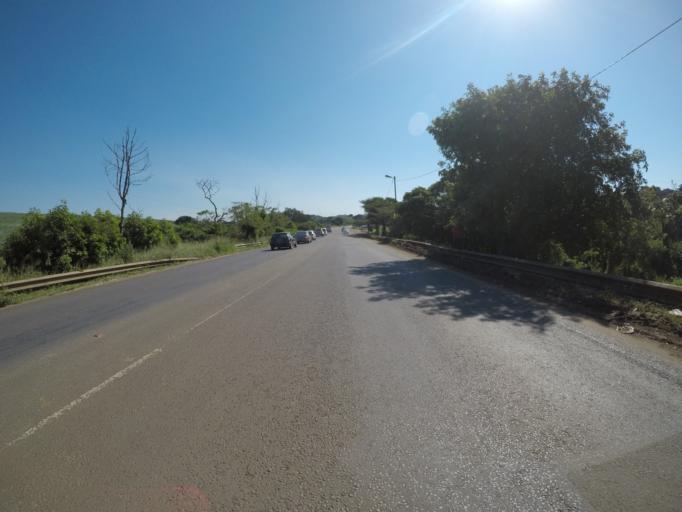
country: ZA
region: KwaZulu-Natal
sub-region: uThungulu District Municipality
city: Empangeni
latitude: -28.7772
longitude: 31.8833
